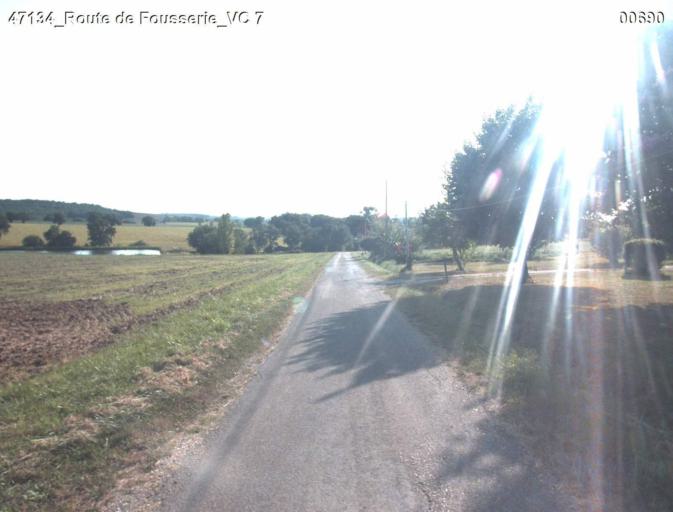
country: FR
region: Aquitaine
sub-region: Departement du Lot-et-Garonne
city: Mezin
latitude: 44.0167
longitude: 0.2729
